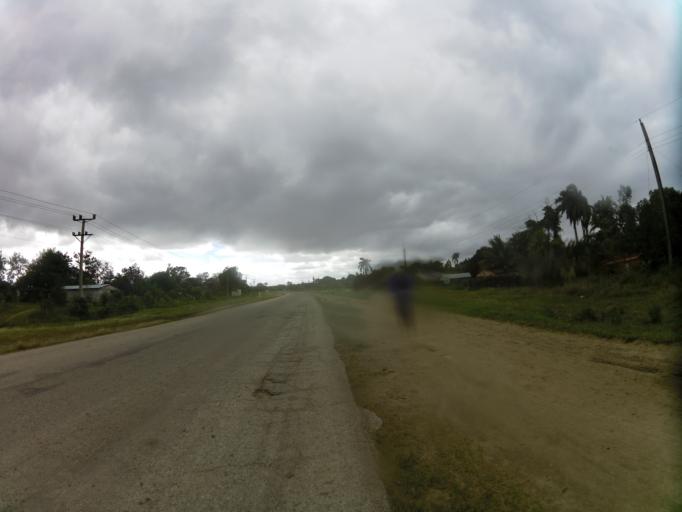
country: CU
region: Las Tunas
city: Las Tunas
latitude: 21.0462
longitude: -76.9321
